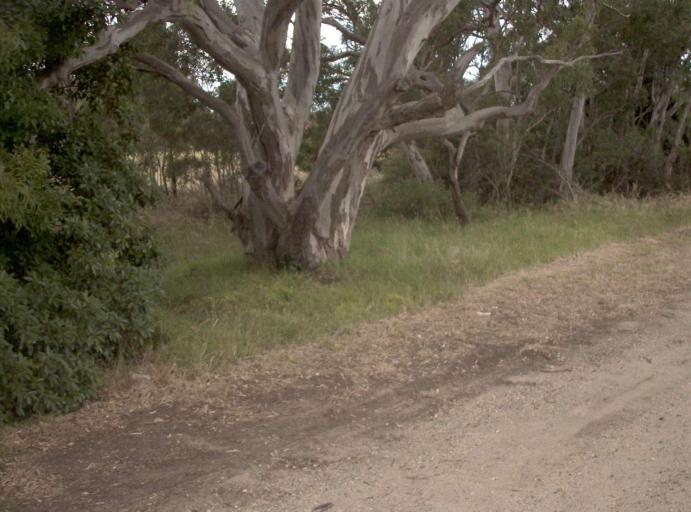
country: AU
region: Victoria
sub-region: Wellington
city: Sale
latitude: -38.1767
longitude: 147.0889
